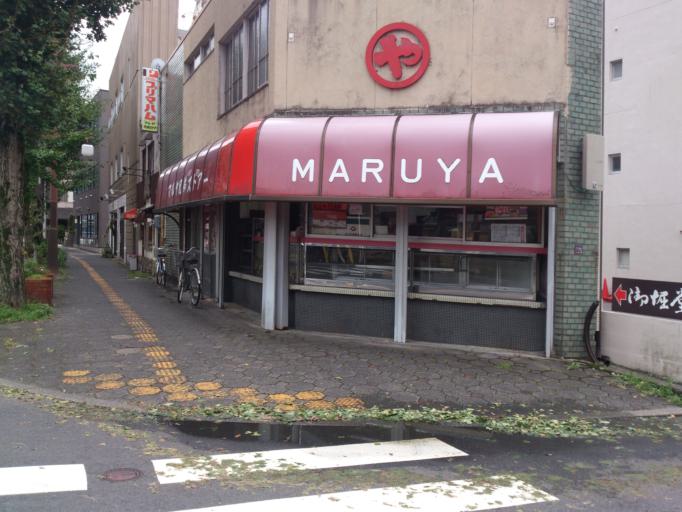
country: JP
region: Yamaguchi
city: Yamaguchi-shi
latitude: 34.1737
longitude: 131.4795
